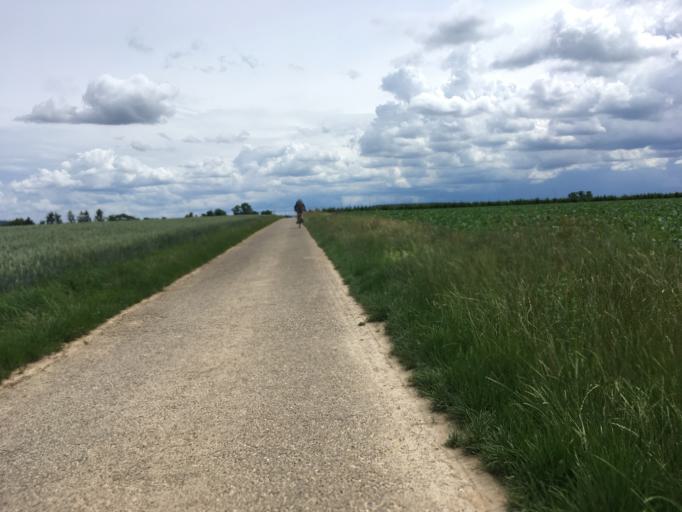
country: DE
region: Baden-Wuerttemberg
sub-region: Regierungsbezirk Stuttgart
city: Bietigheim-Bissingen
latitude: 48.9537
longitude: 9.0938
